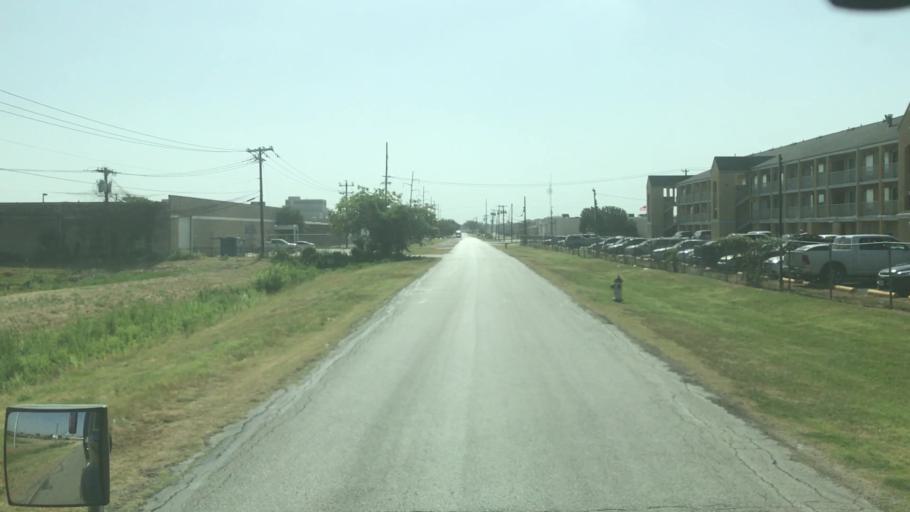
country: US
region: Texas
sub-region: Dallas County
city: Irving
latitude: 32.8369
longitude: -96.9002
